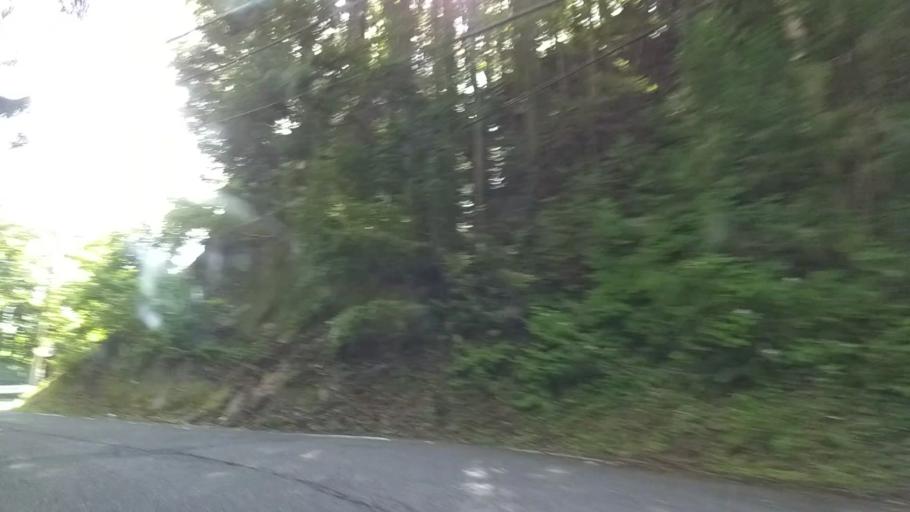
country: JP
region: Yamanashi
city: Uenohara
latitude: 35.5626
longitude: 139.1473
